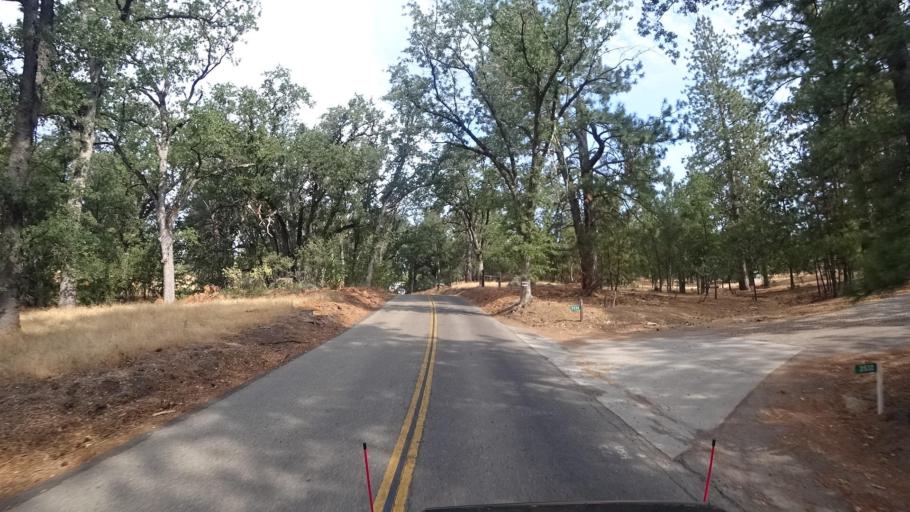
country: US
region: California
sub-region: Mariposa County
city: Midpines
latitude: 37.5096
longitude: -119.8256
